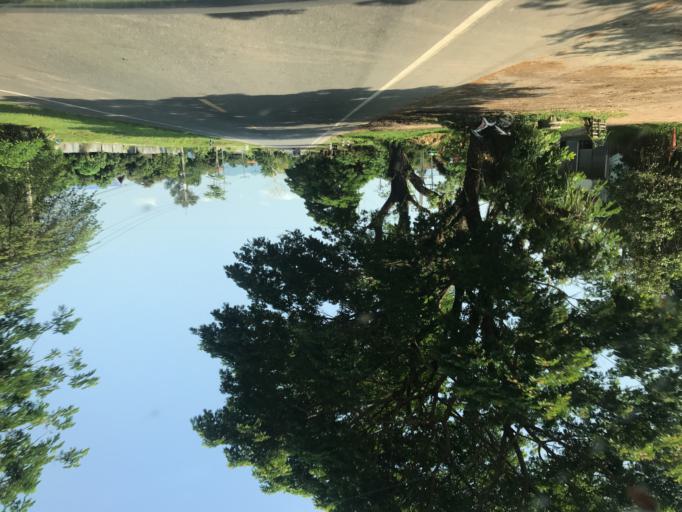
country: TH
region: Phayao
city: Chun
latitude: 19.3945
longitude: 100.1707
